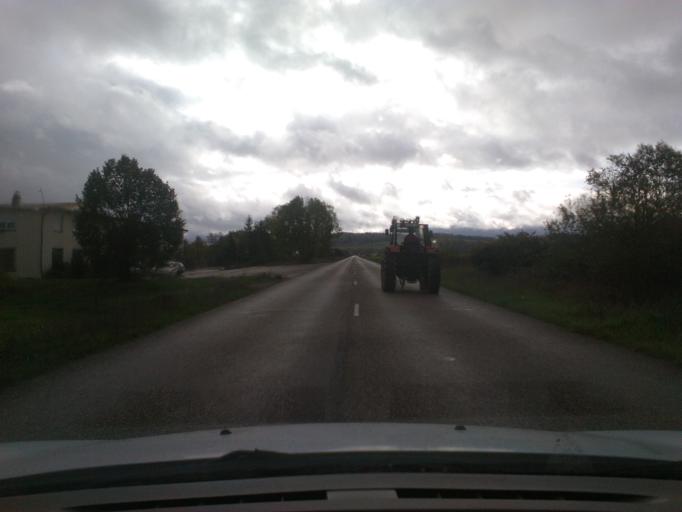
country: FR
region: Lorraine
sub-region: Departement des Vosges
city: Charmes
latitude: 48.3880
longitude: 6.2614
